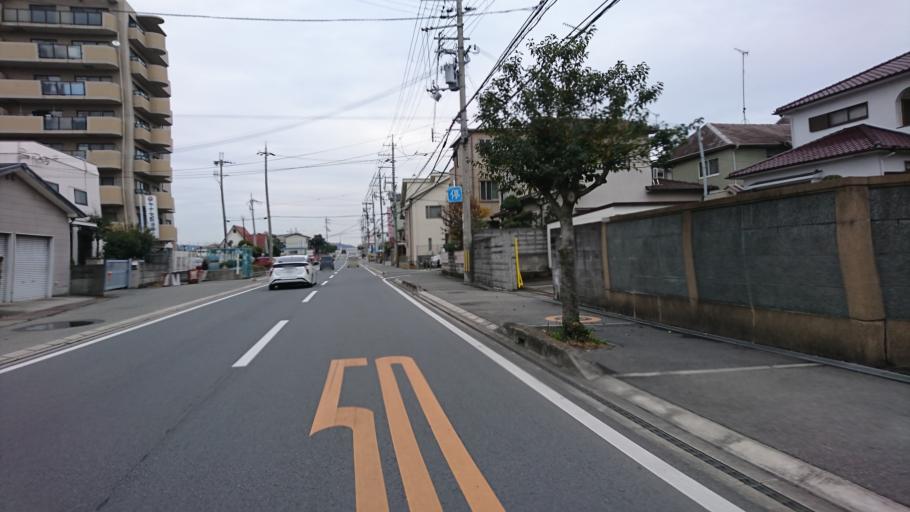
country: JP
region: Hyogo
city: Kakogawacho-honmachi
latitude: 34.7691
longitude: 134.8251
